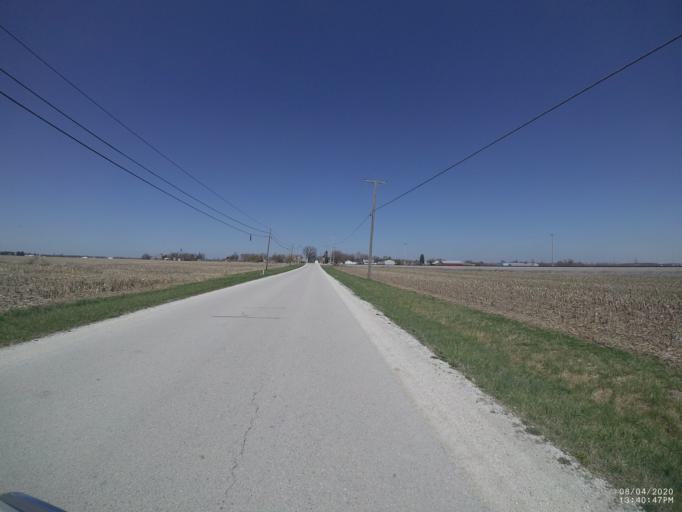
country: US
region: Ohio
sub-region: Sandusky County
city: Gibsonburg
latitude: 41.3344
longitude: -83.2918
